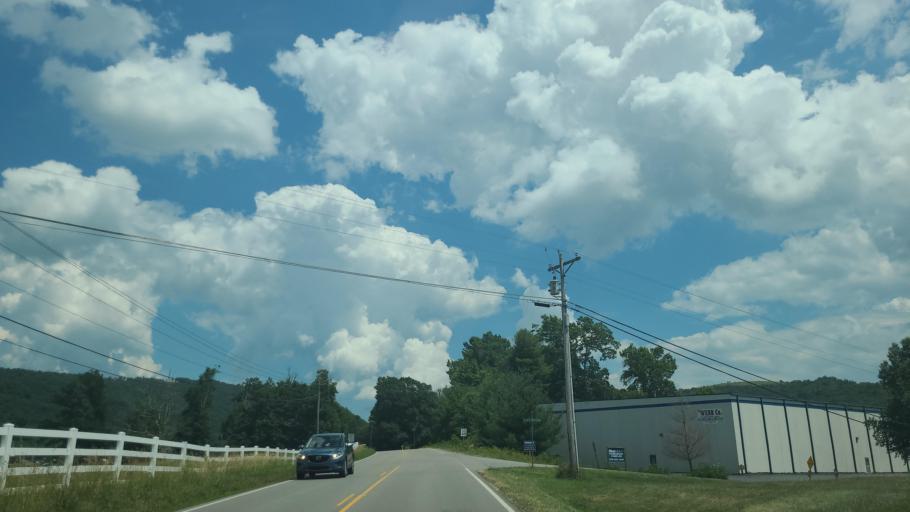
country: US
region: North Carolina
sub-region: Watauga County
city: Boone
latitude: 36.2383
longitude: -81.5215
